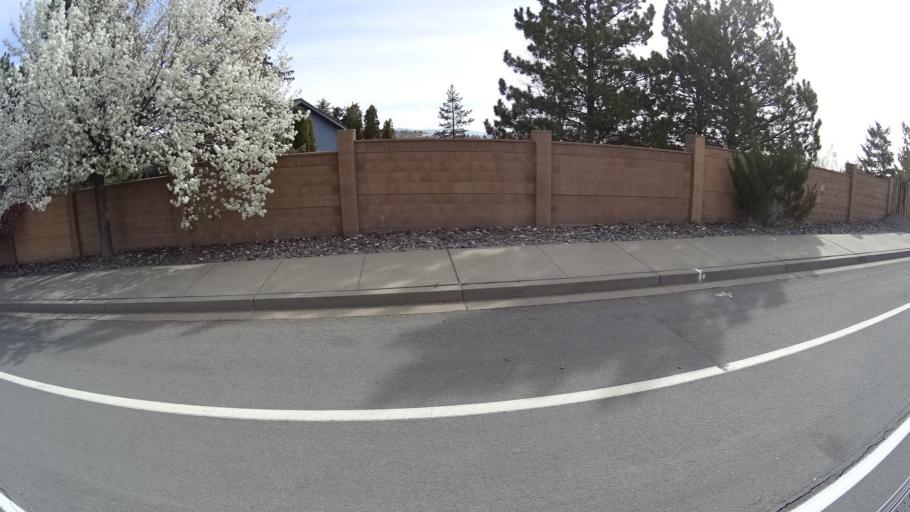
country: US
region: Nevada
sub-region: Washoe County
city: Mogul
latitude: 39.5316
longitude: -119.8941
